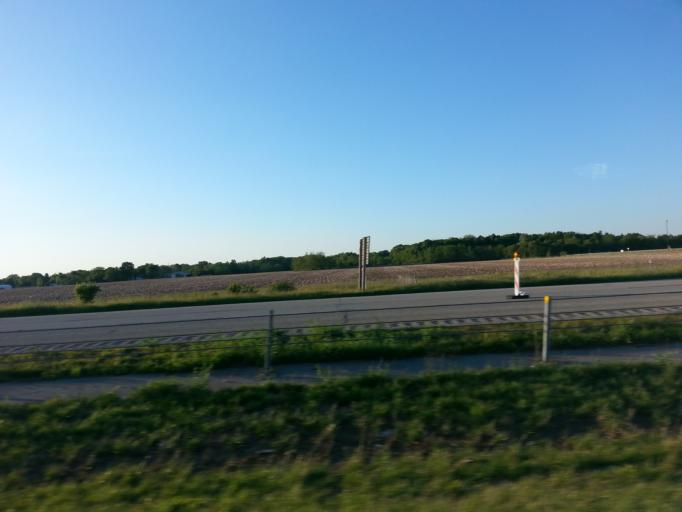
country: US
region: Illinois
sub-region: Vermilion County
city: Oakwood
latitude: 40.1275
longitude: -87.7489
